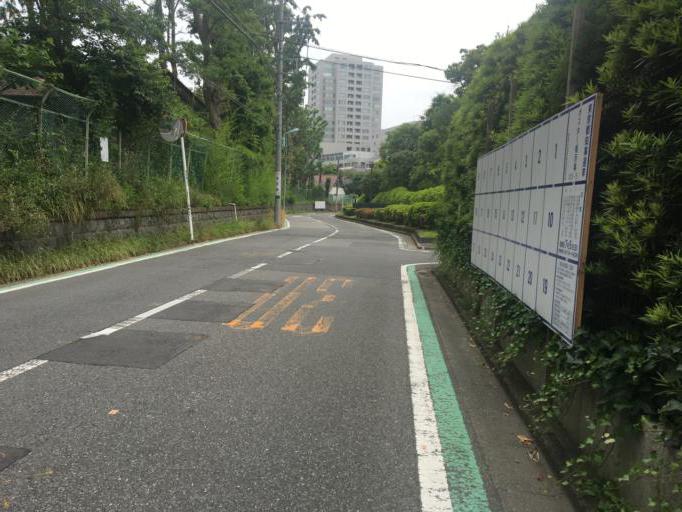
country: JP
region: Tokyo
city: Tokyo
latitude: 35.7166
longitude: 139.7084
